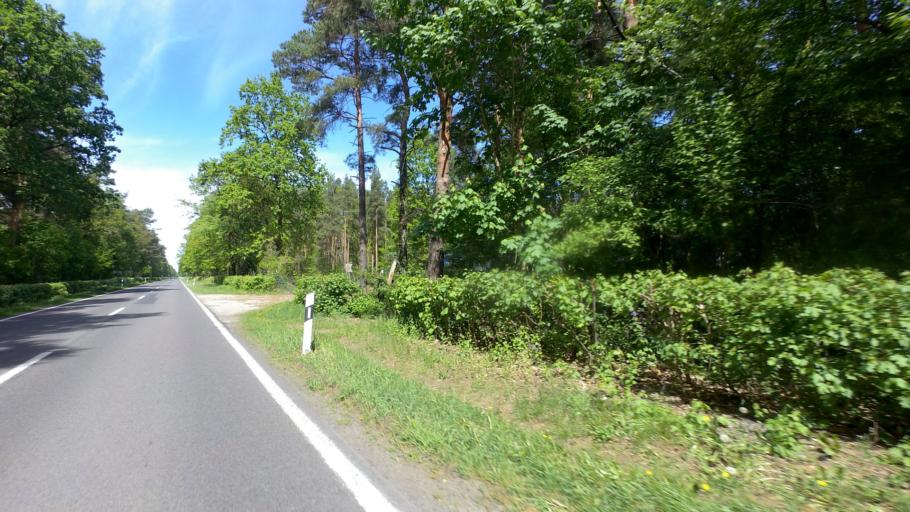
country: DE
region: Brandenburg
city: Sperenberg
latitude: 52.1050
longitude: 13.3729
